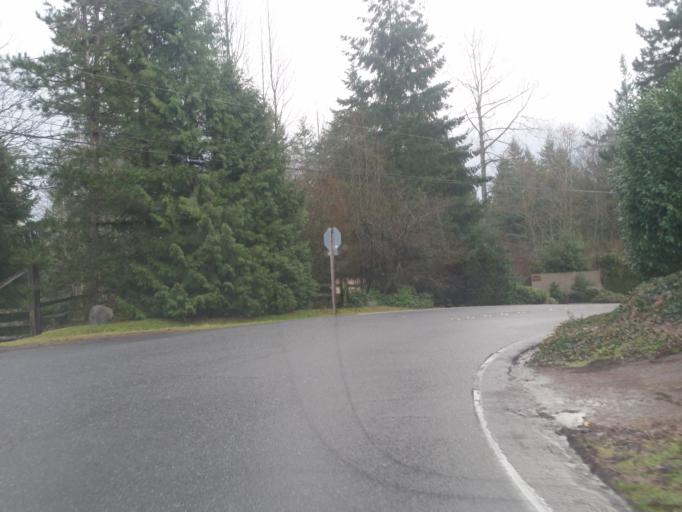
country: US
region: Washington
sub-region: Snohomish County
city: Brier
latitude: 47.7918
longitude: -122.2641
